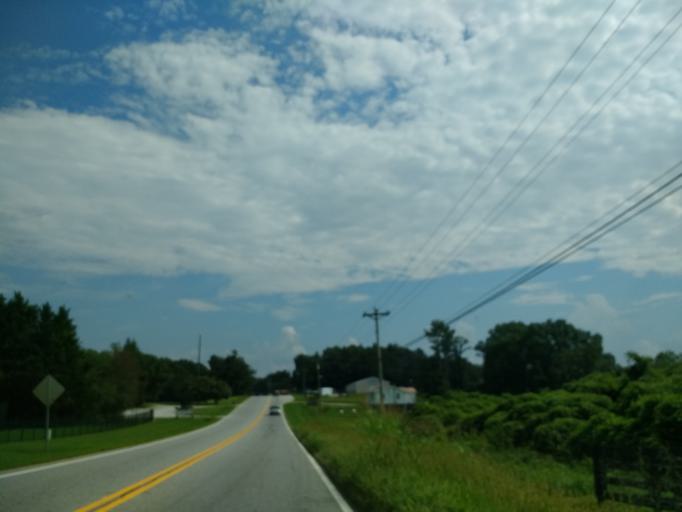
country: US
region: Georgia
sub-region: Hall County
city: Gainesville
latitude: 34.4357
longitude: -83.8085
